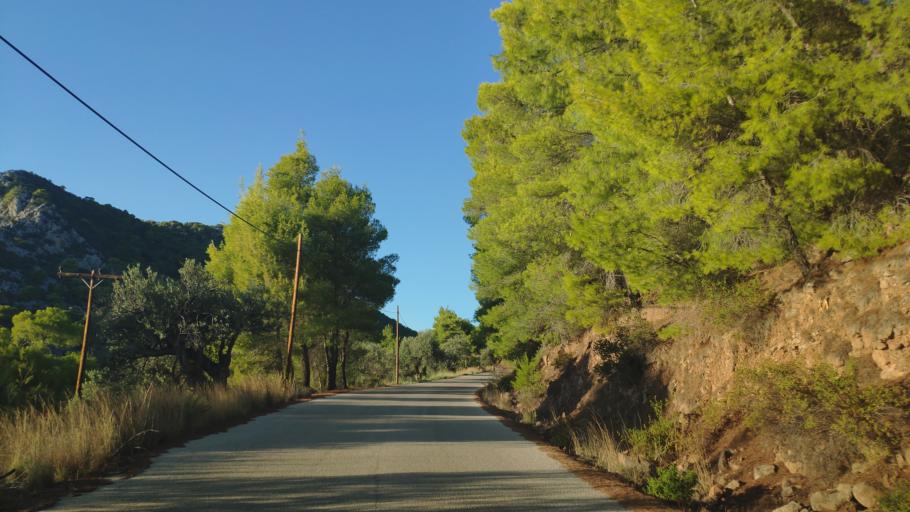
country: GR
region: Attica
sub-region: Nomos Piraios
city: Megalochori
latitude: 37.6085
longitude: 23.3290
